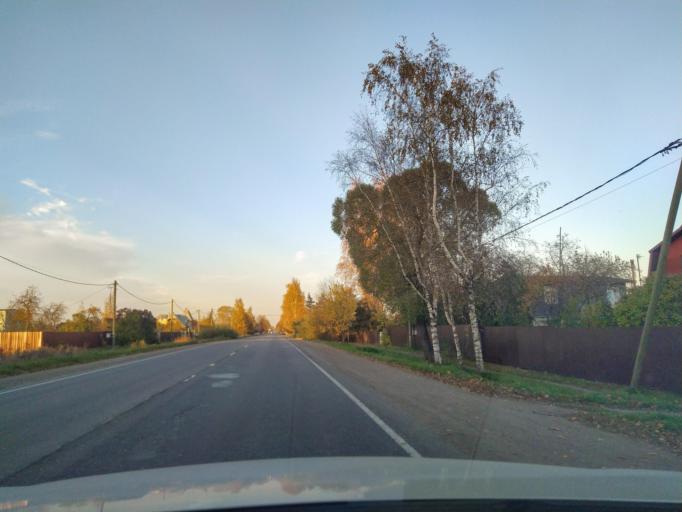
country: RU
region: Leningrad
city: Maloye Verevo
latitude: 59.6125
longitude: 30.2003
